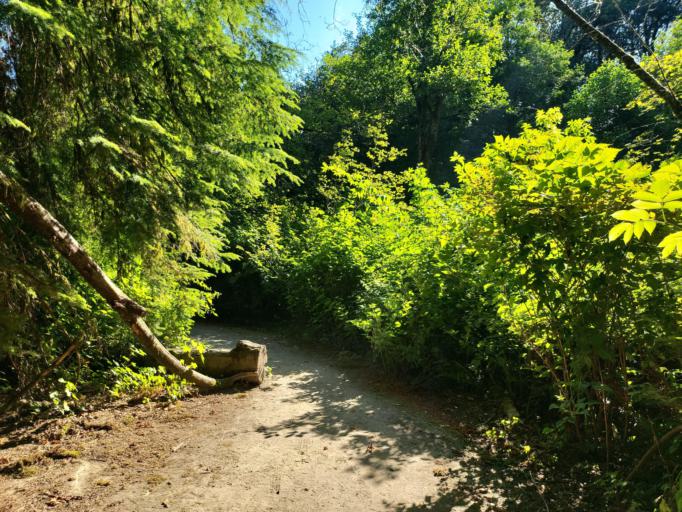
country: US
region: Washington
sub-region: King County
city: Newcastle
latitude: 47.5506
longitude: -122.1636
